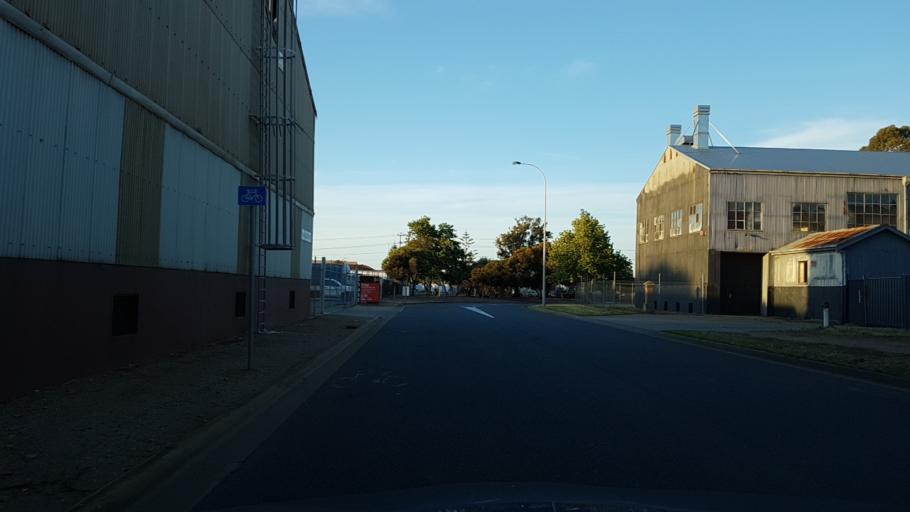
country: AU
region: South Australia
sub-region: Charles Sturt
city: Woodville North
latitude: -34.8610
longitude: 138.5377
